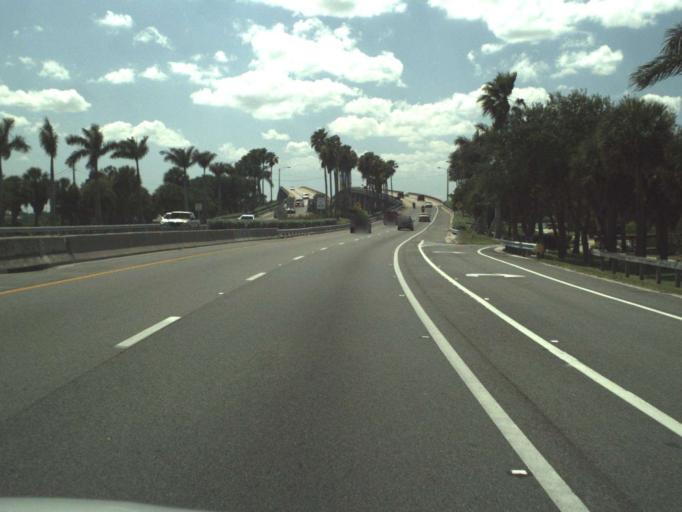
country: US
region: Florida
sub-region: Brevard County
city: Rockledge
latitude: 28.3565
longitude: -80.7121
